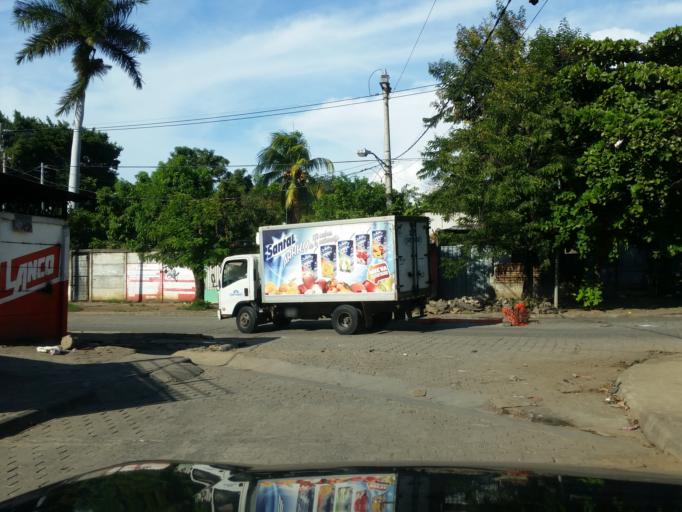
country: NI
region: Managua
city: Managua
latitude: 12.1147
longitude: -86.2342
